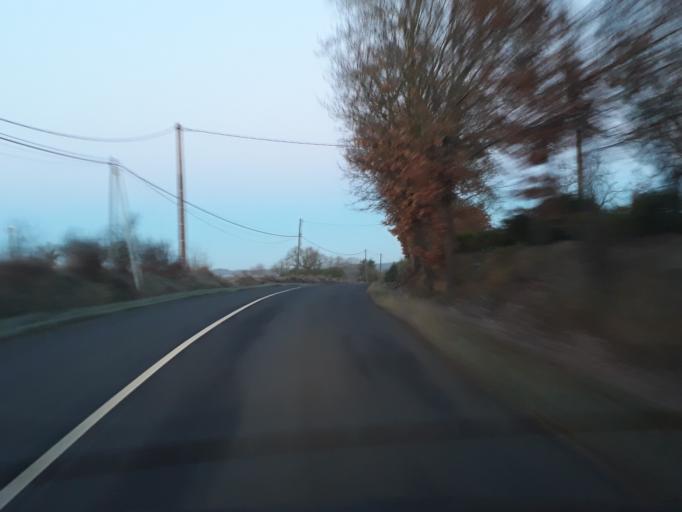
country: FR
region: Midi-Pyrenees
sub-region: Departement du Gers
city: Samatan
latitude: 43.4775
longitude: 0.9432
